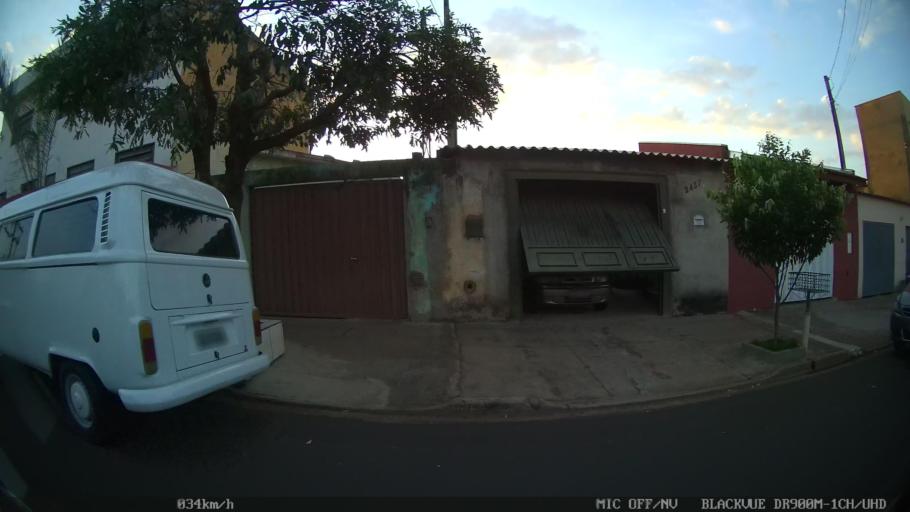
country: BR
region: Sao Paulo
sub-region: Ribeirao Preto
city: Ribeirao Preto
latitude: -21.1407
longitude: -47.8230
